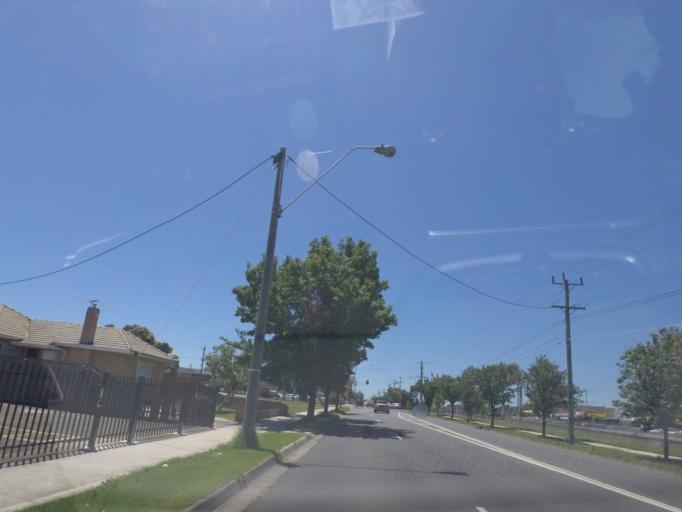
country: AU
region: Victoria
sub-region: Whittlesea
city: Lalor
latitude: -37.6736
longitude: 145.0150
